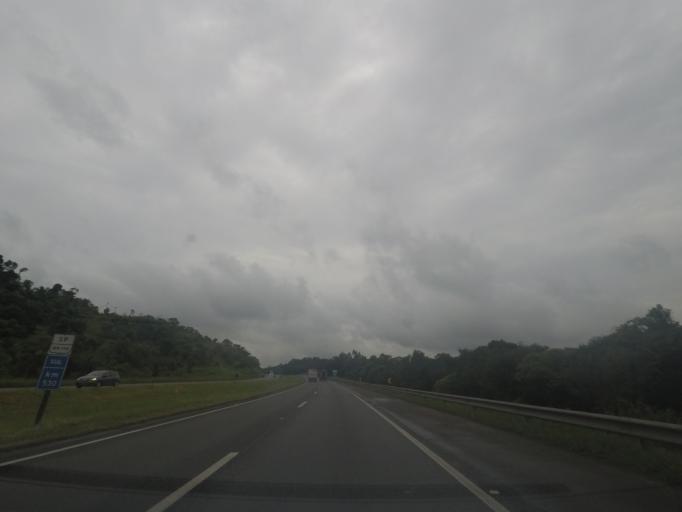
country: BR
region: Sao Paulo
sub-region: Cajati
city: Cajati
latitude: -24.9425
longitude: -48.3092
